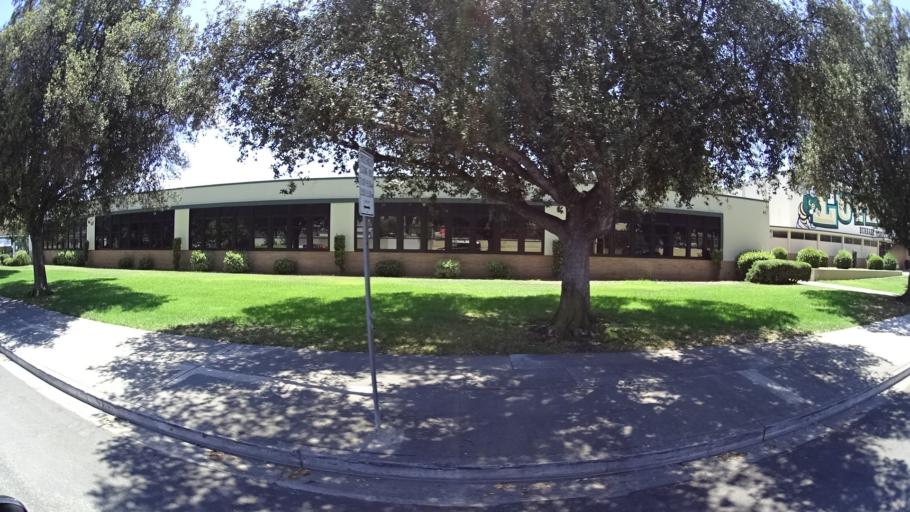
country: US
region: California
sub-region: Los Angeles County
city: North Hollywood
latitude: 34.1811
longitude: -118.3521
